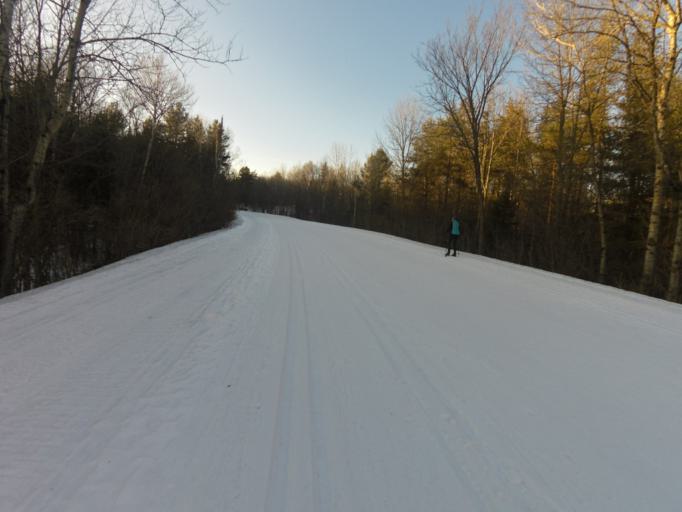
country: CA
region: Quebec
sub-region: Outaouais
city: Gatineau
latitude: 45.5147
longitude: -75.8237
